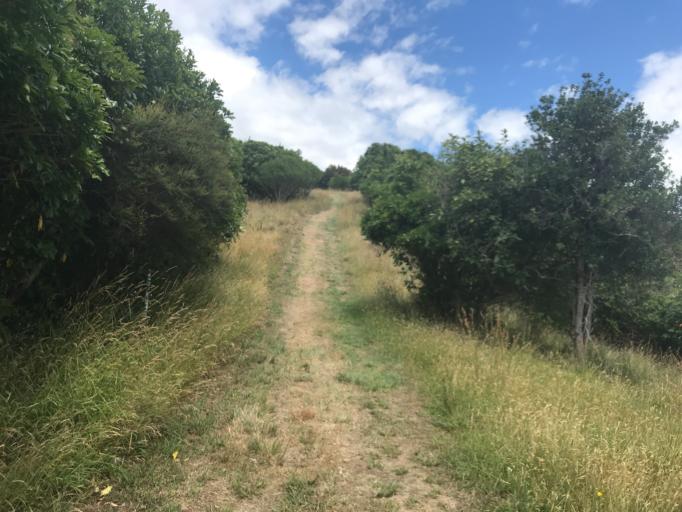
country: NZ
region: Marlborough
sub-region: Marlborough District
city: Picton
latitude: -41.2128
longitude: 173.9966
